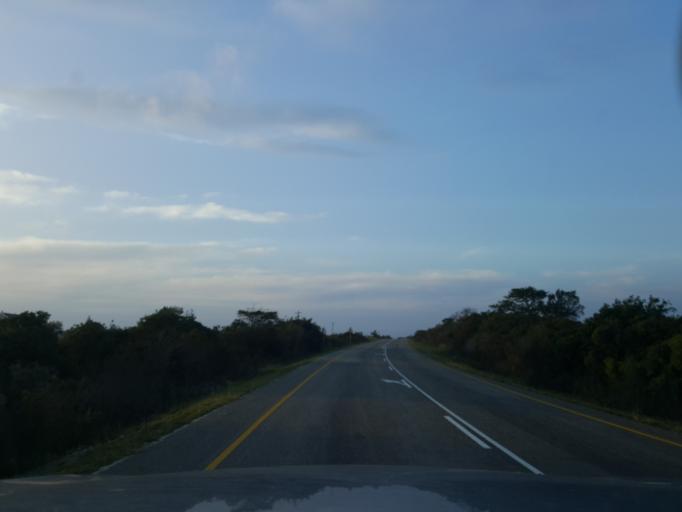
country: ZA
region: Eastern Cape
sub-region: Cacadu District Municipality
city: Grahamstown
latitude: -33.4933
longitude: 26.4859
